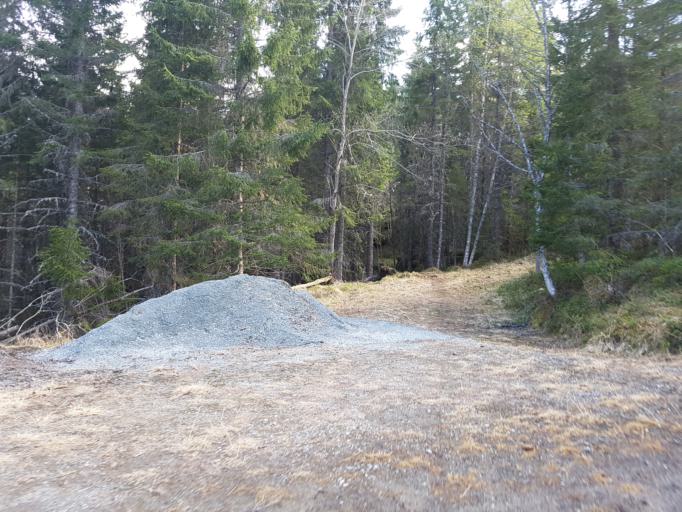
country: NO
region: Sor-Trondelag
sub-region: Trondheim
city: Trondheim
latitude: 63.4407
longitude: 10.2888
